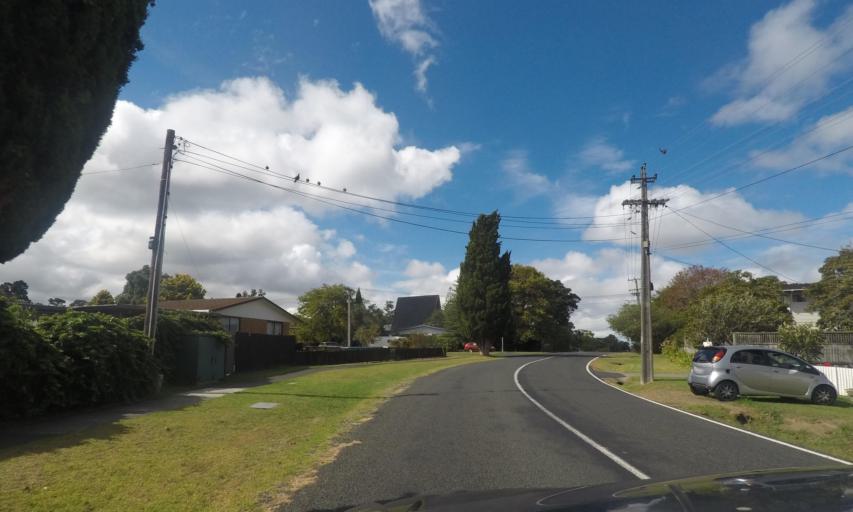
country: NZ
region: Auckland
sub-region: Auckland
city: Rosebank
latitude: -36.7806
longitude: 174.6552
